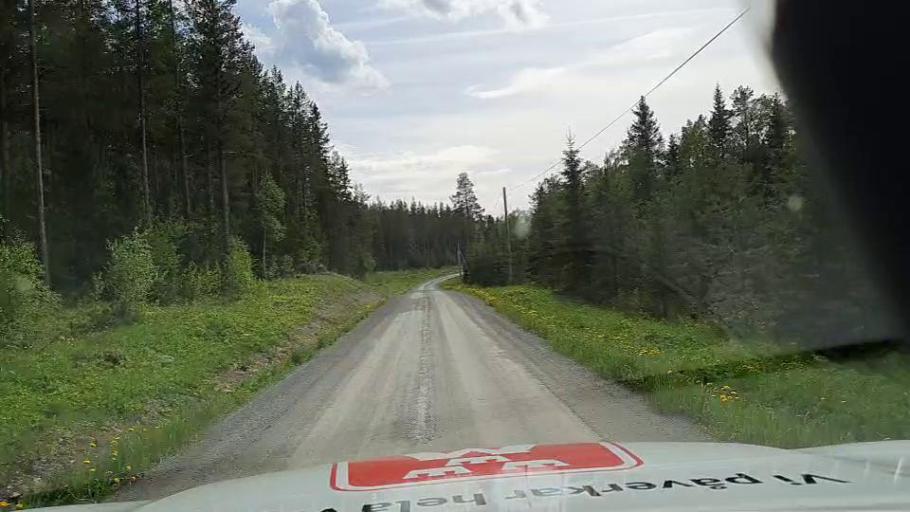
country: SE
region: Jaemtland
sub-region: OEstersunds Kommun
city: Brunflo
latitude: 62.9856
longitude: 14.7119
